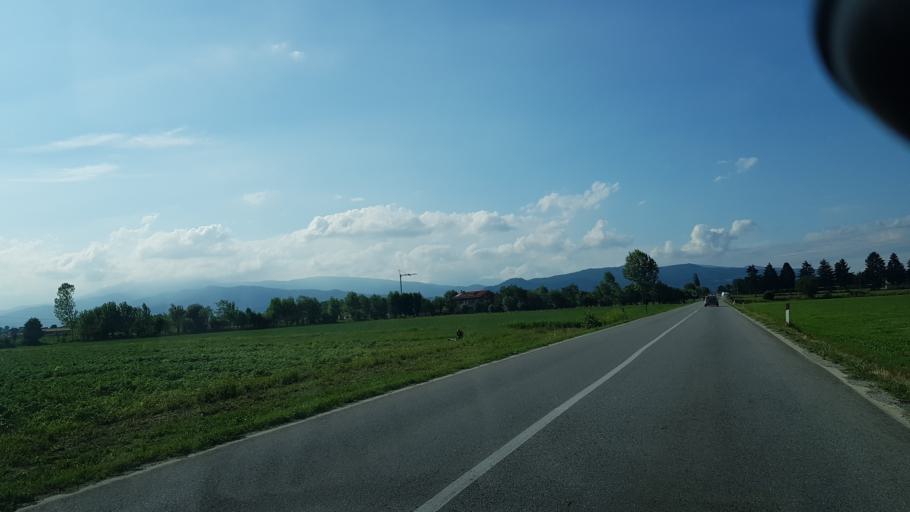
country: IT
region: Piedmont
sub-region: Provincia di Cuneo
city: Roata Rossi
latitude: 44.4587
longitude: 7.5199
